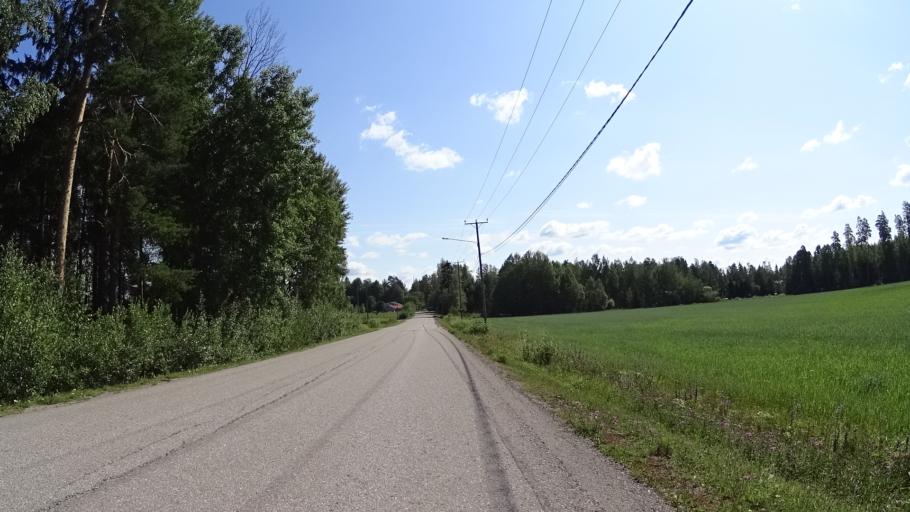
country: FI
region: Uusimaa
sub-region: Helsinki
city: Jaervenpaeae
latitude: 60.4469
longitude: 25.0956
